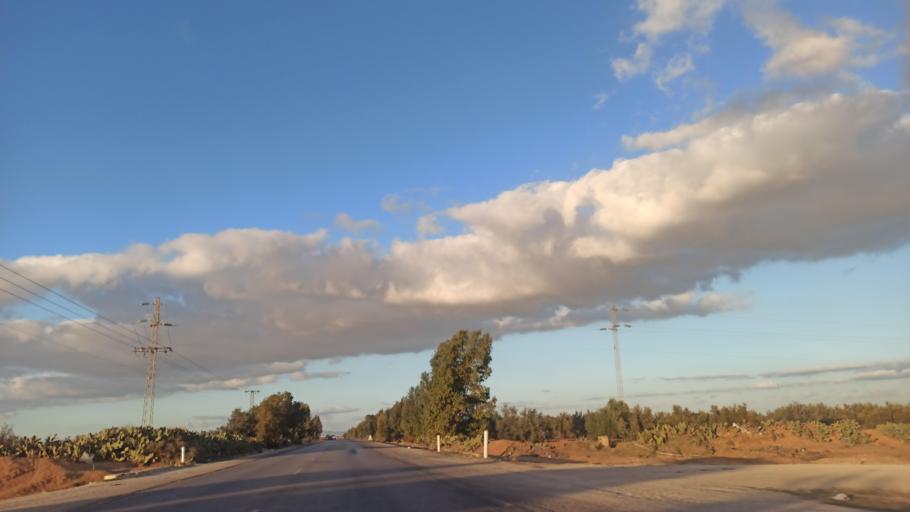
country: TN
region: Susah
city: Sidi Bou Ali
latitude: 35.9720
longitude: 10.3092
